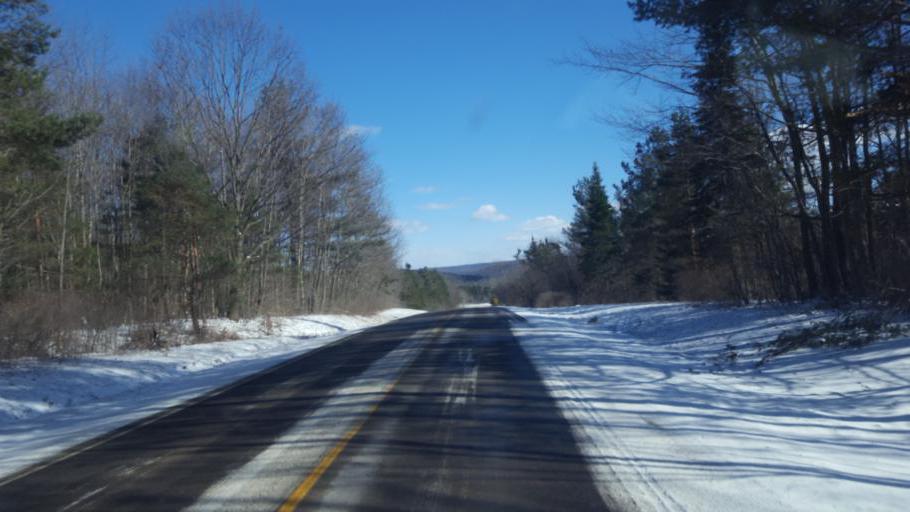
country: US
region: New York
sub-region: Allegany County
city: Belmont
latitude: 42.1811
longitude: -78.0777
